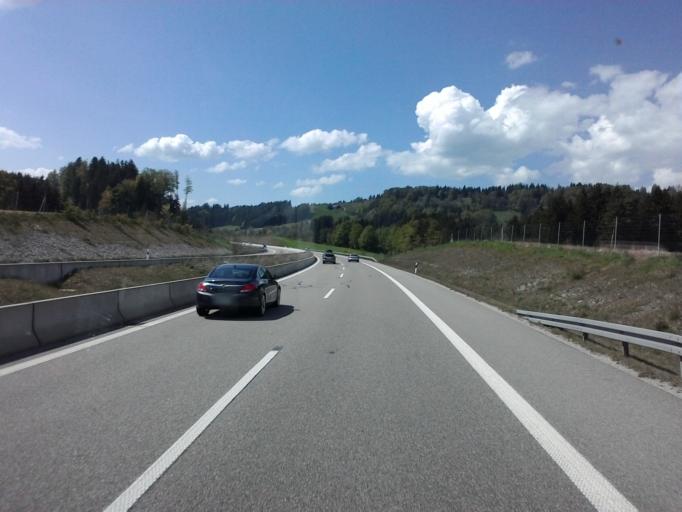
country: DE
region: Bavaria
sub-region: Swabia
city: Hopferau
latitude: 47.6247
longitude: 10.6575
